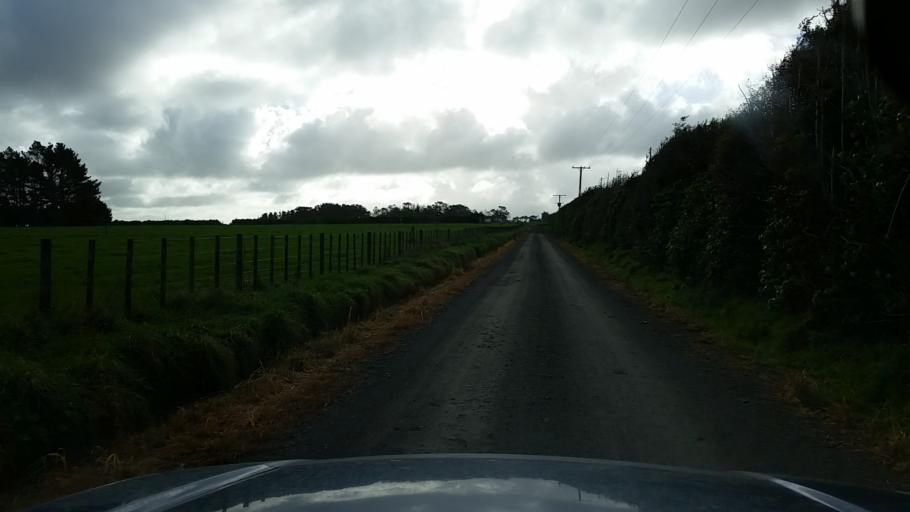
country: NZ
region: Taranaki
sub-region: South Taranaki District
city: Hawera
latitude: -39.5166
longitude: 174.3276
